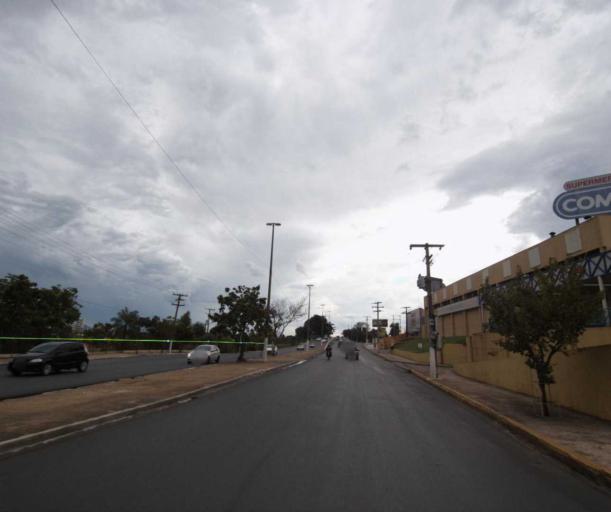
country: BR
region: Mato Grosso
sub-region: Cuiaba
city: Cuiaba
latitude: -15.6060
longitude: -56.0790
